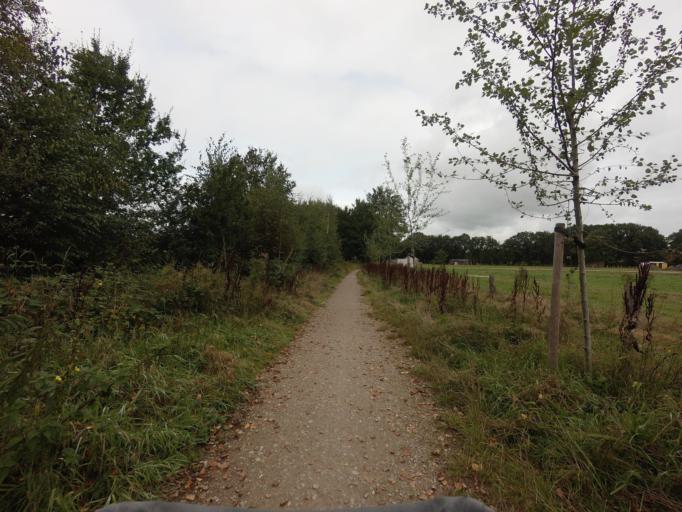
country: DE
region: North Rhine-Westphalia
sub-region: Regierungsbezirk Munster
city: Gronau
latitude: 52.2269
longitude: 7.0321
